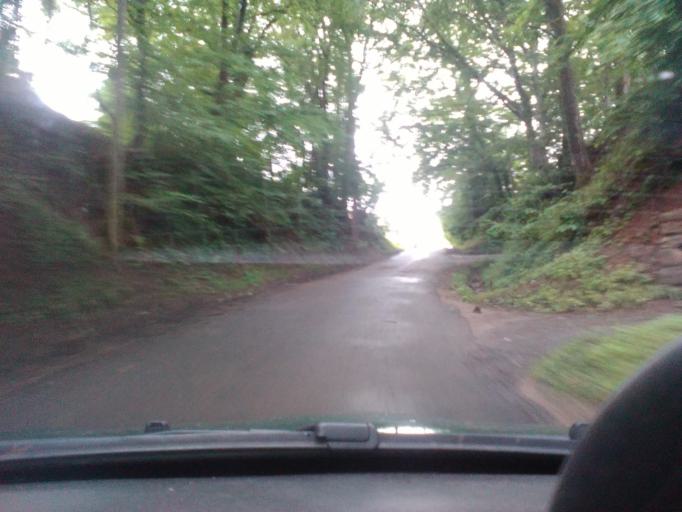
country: FR
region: Lorraine
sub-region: Departement des Vosges
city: Saint-Michel-sur-Meurthe
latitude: 48.3253
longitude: 6.9184
